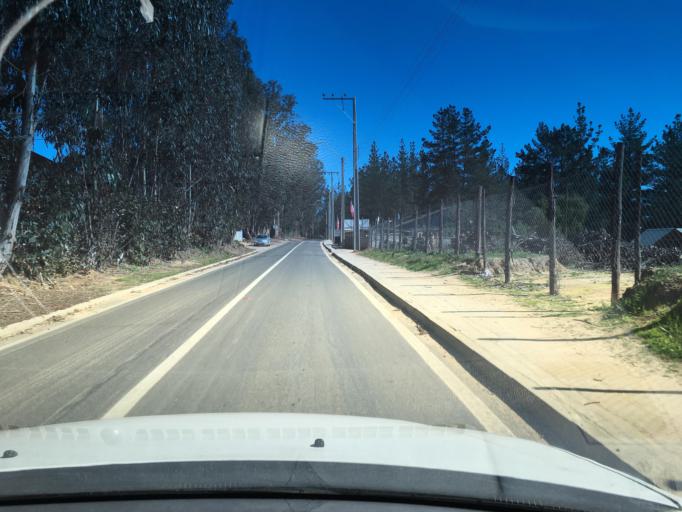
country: CL
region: Valparaiso
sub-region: San Antonio Province
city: El Tabo
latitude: -33.4214
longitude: -71.6269
